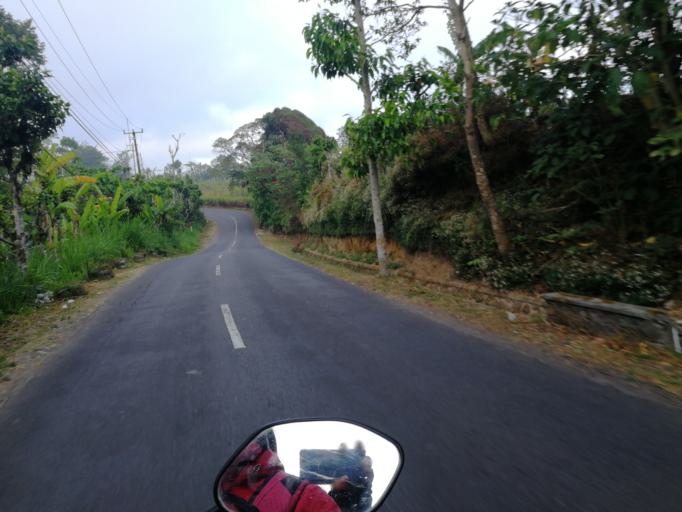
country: ID
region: Bali
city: Banjar Ambengan
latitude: -8.2284
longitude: 115.2456
